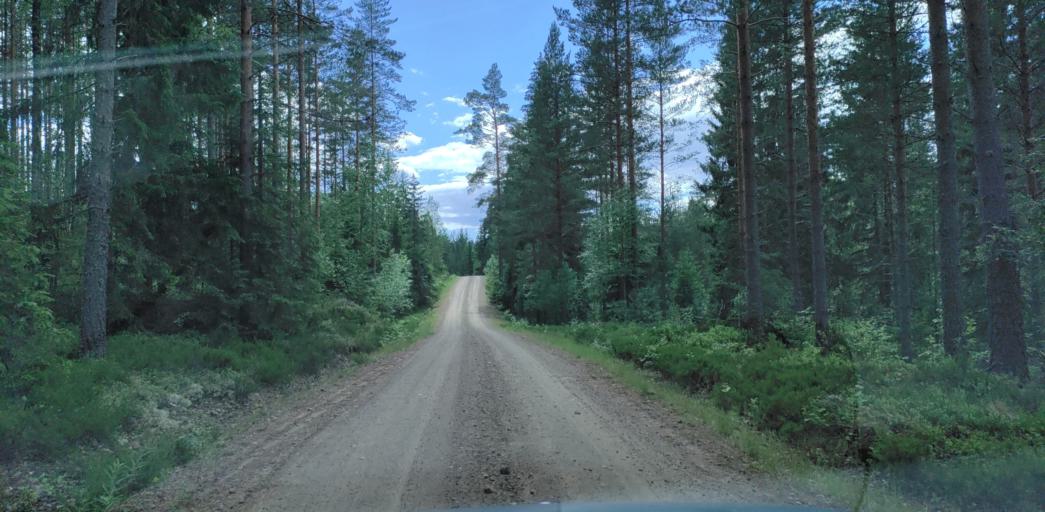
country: SE
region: Vaermland
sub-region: Hagfors Kommun
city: Ekshaerad
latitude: 60.0795
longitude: 13.2926
